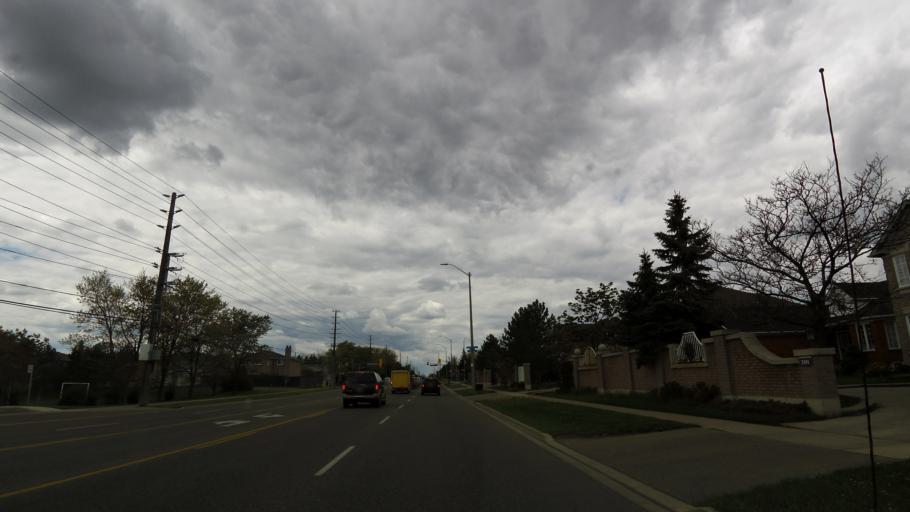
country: CA
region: Ontario
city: Mississauga
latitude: 43.5800
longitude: -79.6880
